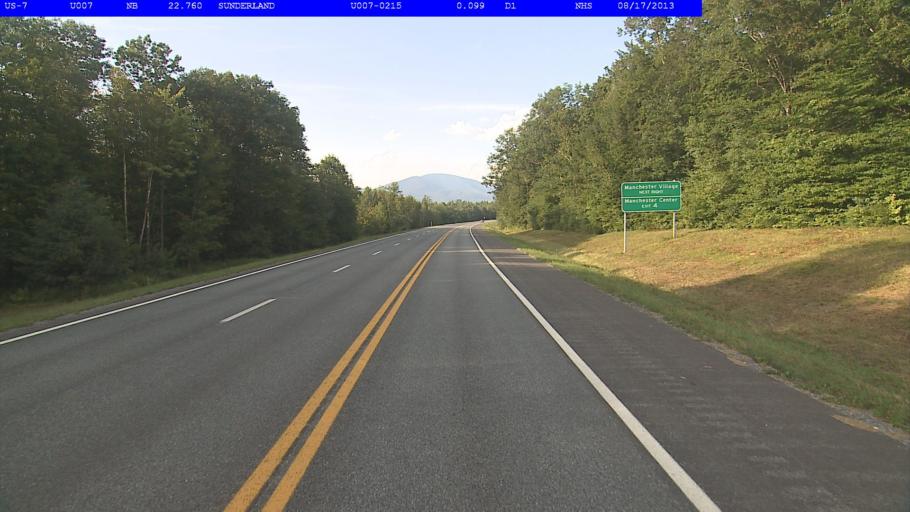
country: US
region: Vermont
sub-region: Bennington County
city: Arlington
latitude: 43.0271
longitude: -73.1397
